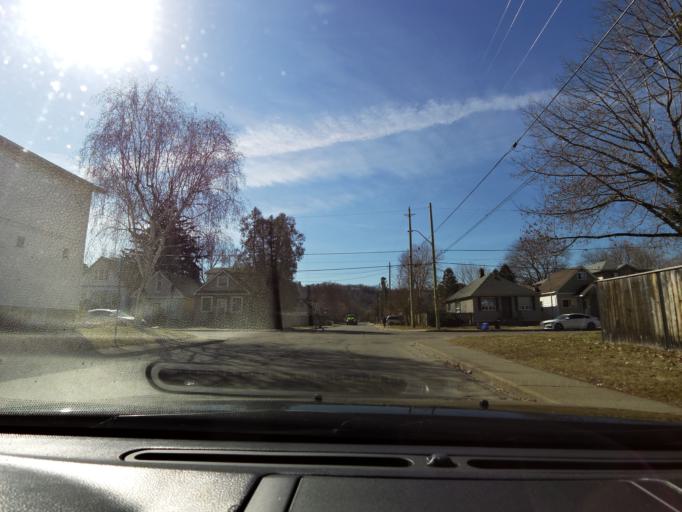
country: CA
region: Ontario
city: Ancaster
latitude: 43.2545
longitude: -79.9237
